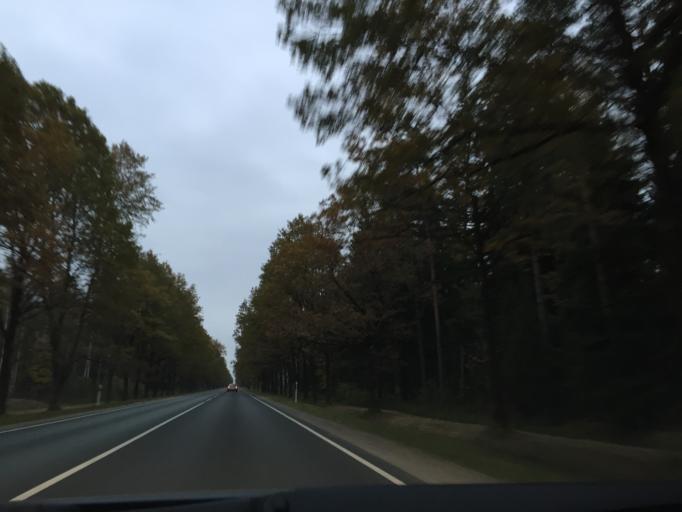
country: LV
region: Ozolnieku
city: Ozolnieki
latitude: 56.7005
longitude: 23.8115
